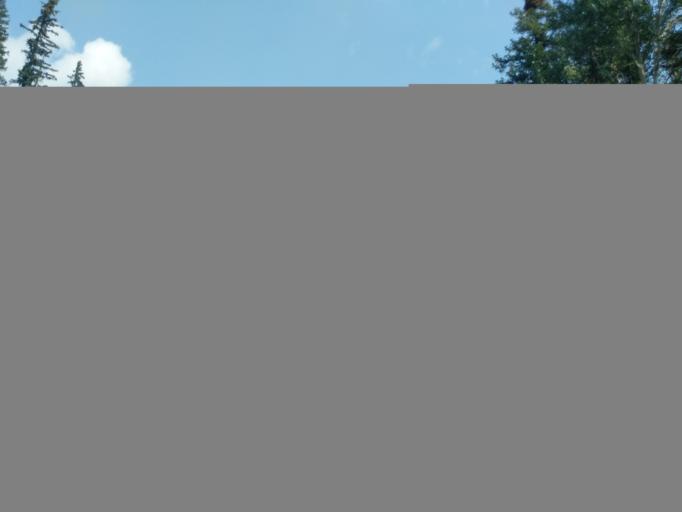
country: CA
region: Alberta
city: Banff
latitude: 51.1679
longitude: -115.6756
